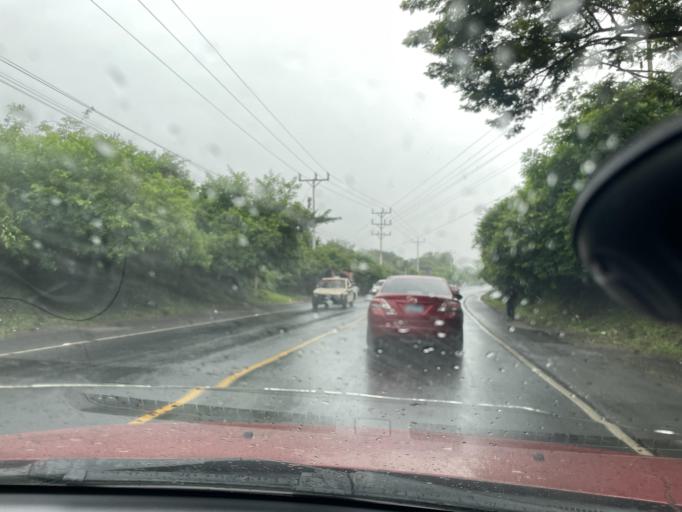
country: SV
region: Morazan
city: Jocoro
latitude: 13.5624
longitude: -88.1024
